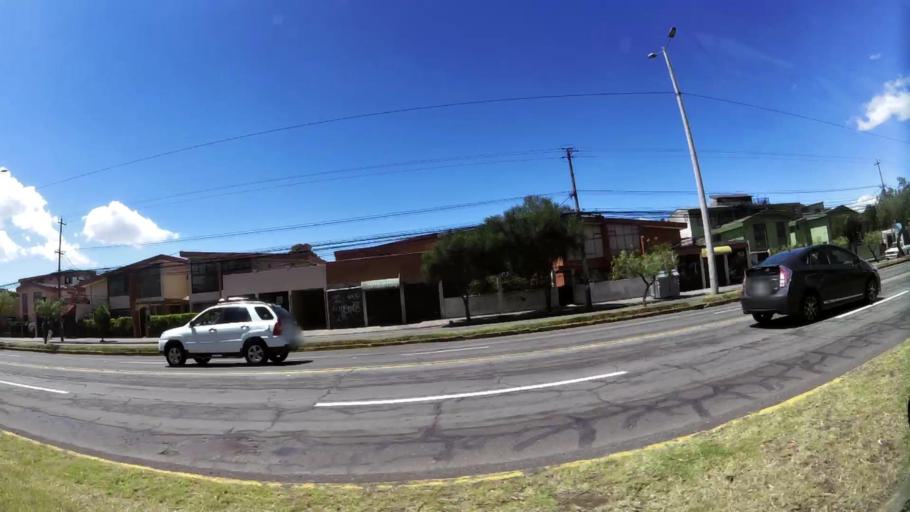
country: EC
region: Pichincha
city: Quito
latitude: -0.1495
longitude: -78.4841
